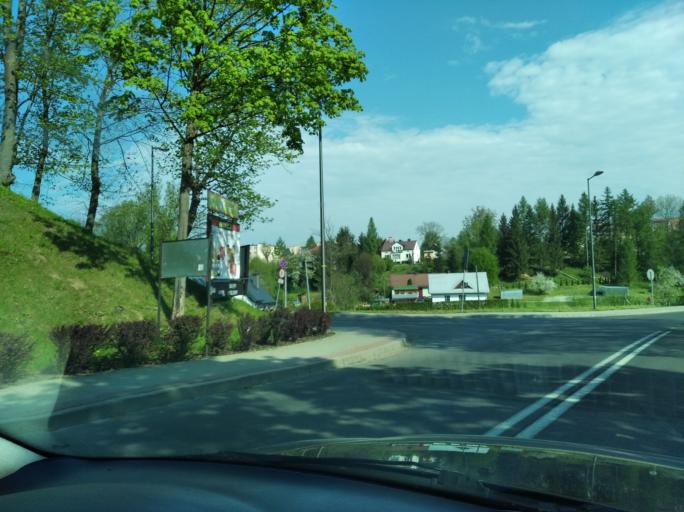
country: PL
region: Subcarpathian Voivodeship
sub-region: Powiat rzeszowski
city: Dynow
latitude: 49.8162
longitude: 22.2339
